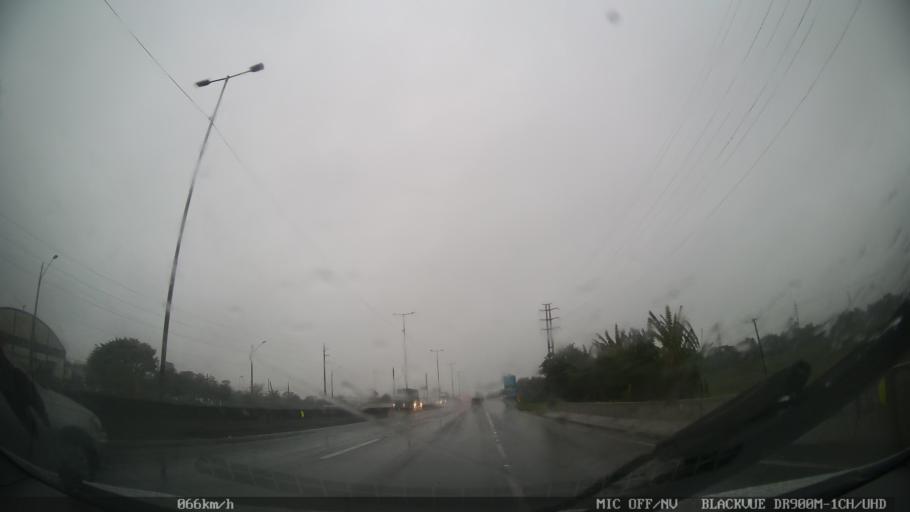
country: BR
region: Santa Catarina
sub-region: Itajai
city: Itajai
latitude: -26.9074
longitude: -48.7136
